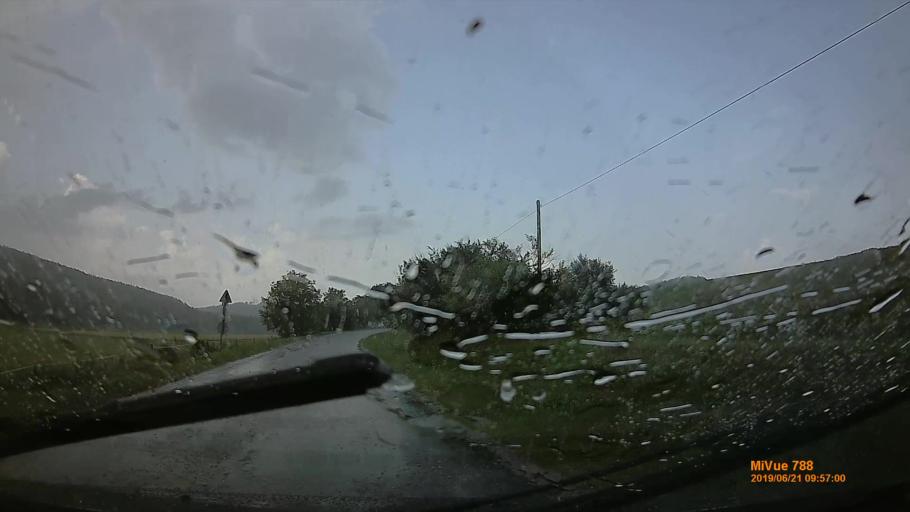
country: HU
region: Baranya
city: Buekkoesd
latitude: 46.2228
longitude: 17.9760
